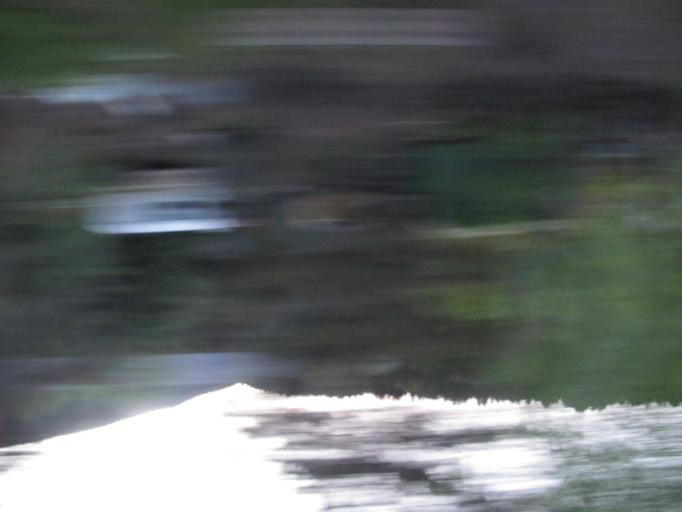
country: NO
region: Oppland
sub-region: Ringebu
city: Ringebu
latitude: 61.5504
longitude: 10.0570
